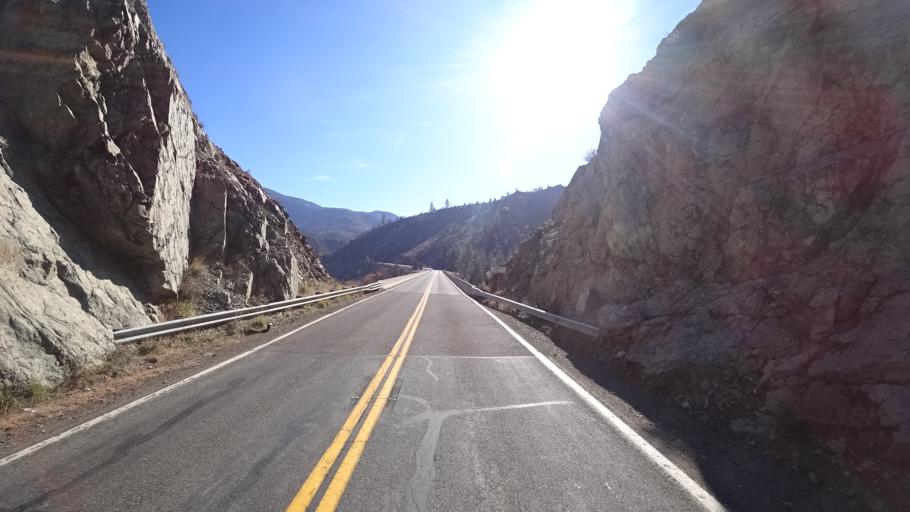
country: US
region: California
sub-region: Siskiyou County
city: Yreka
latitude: 41.8229
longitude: -122.5932
